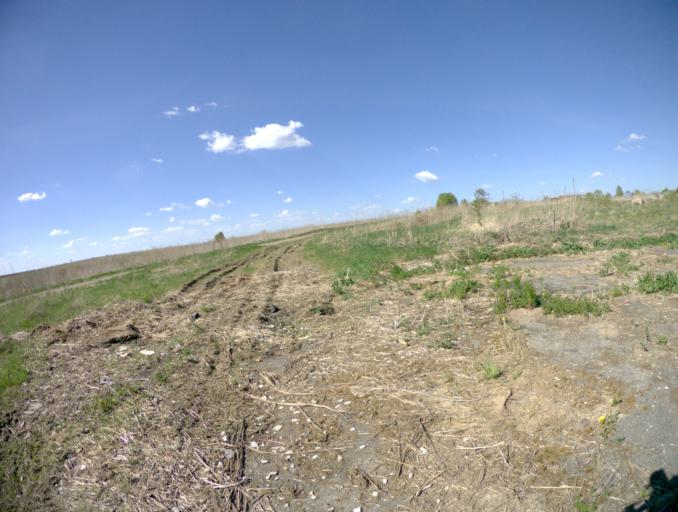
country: RU
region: Vladimir
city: Vladimir
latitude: 56.3018
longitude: 40.2852
